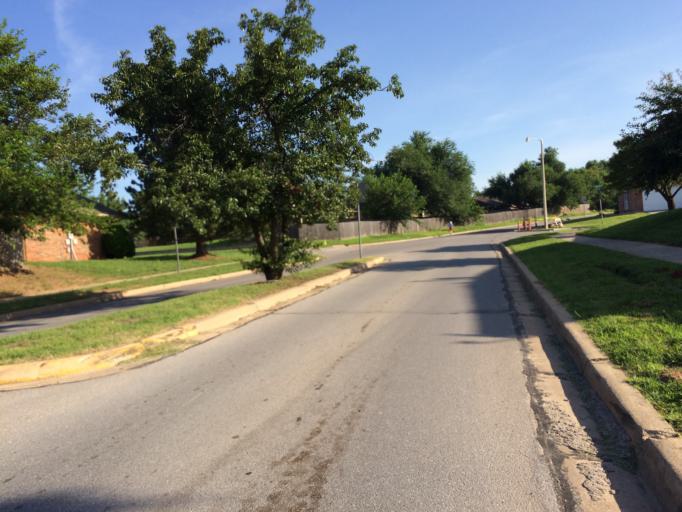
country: US
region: Oklahoma
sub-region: Cleveland County
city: Norman
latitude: 35.2185
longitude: -97.5049
